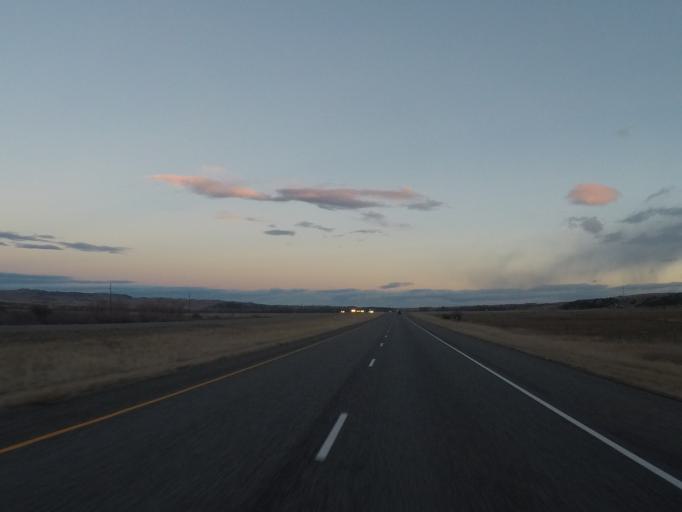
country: US
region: Montana
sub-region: Sweet Grass County
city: Big Timber
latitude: 45.7910
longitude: -109.8287
